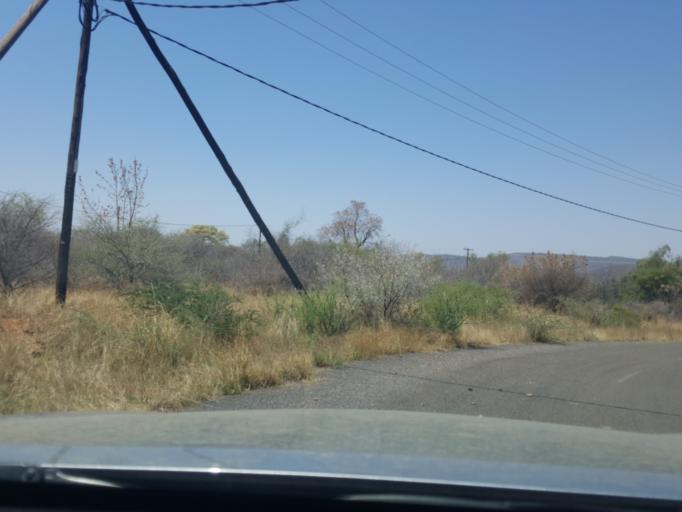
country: BW
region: South East
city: Lobatse
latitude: -25.1899
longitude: 25.6754
